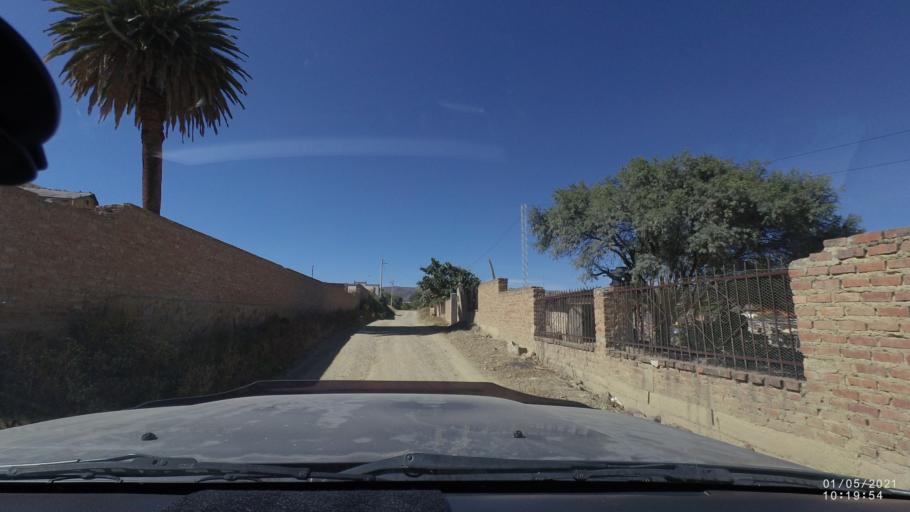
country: BO
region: Cochabamba
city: Capinota
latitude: -17.5601
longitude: -66.2053
